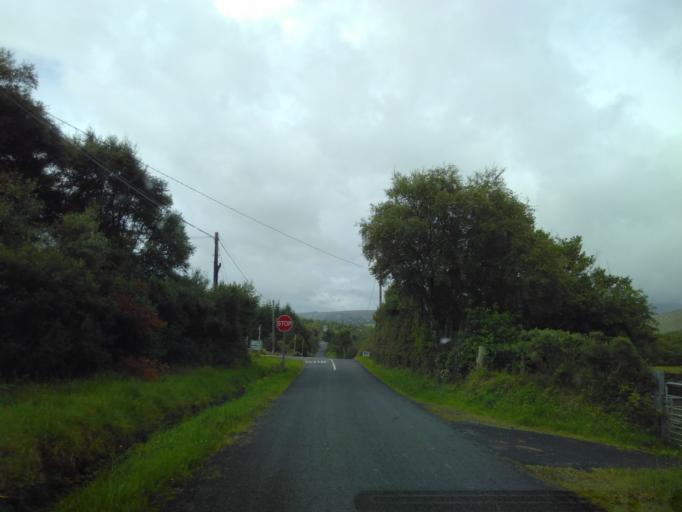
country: IE
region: Ulster
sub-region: County Donegal
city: Dunlewy
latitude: 54.9786
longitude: -7.9300
